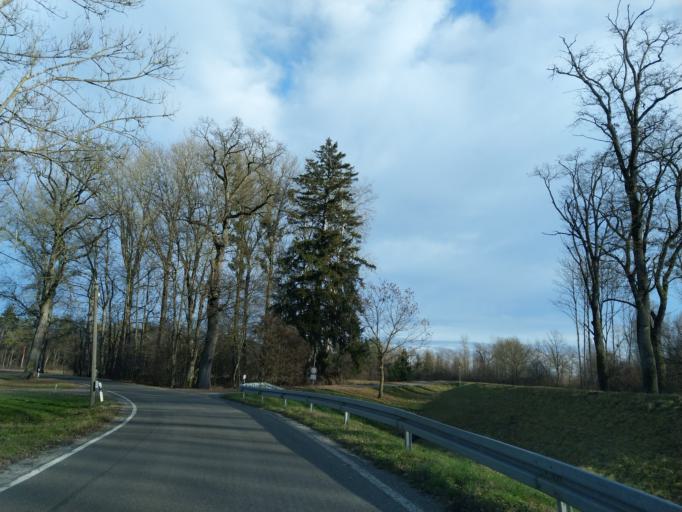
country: DE
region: Bavaria
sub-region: Lower Bavaria
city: Moos
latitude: 48.7773
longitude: 12.9637
